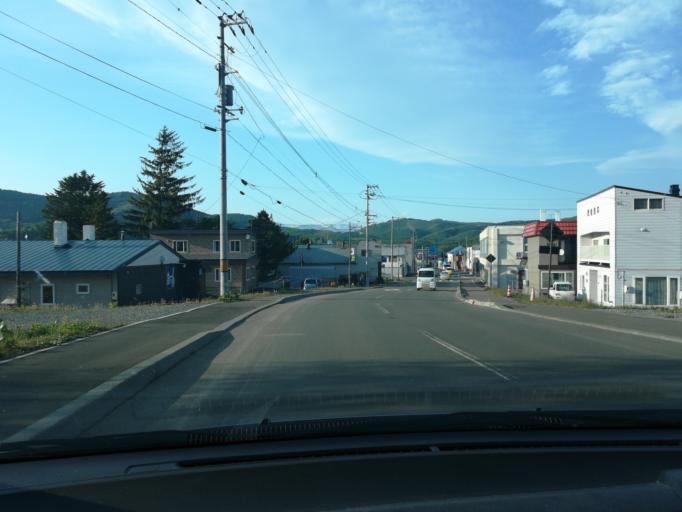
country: JP
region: Hokkaido
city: Shimo-furano
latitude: 43.1620
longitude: 142.5675
